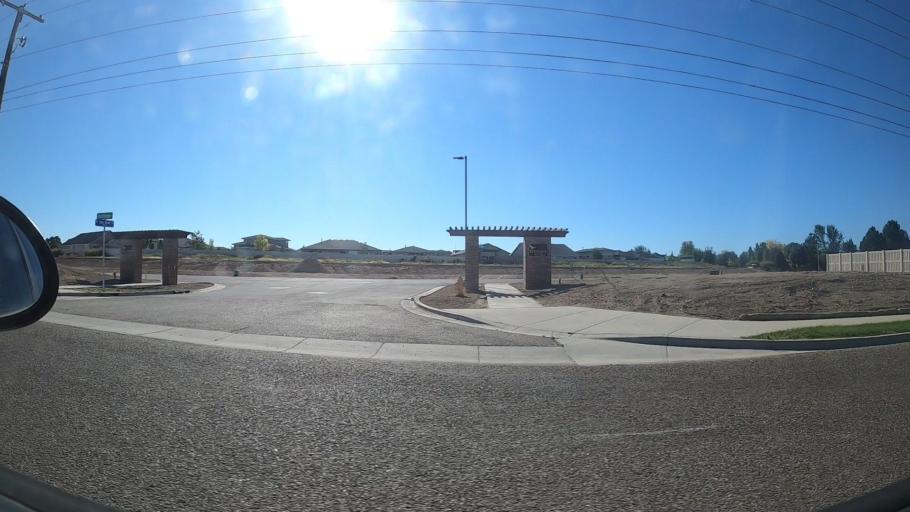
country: US
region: Idaho
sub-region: Canyon County
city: Nampa
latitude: 43.5532
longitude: -116.6127
